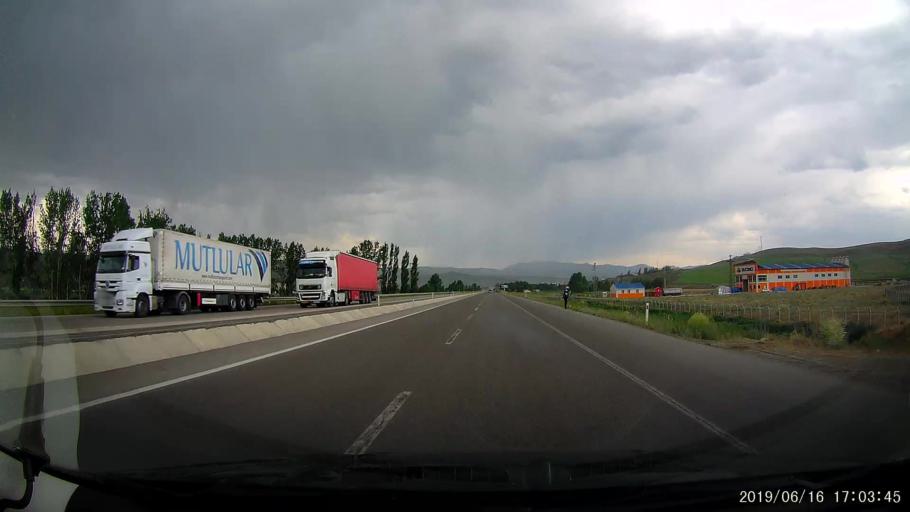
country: TR
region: Erzurum
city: Askale
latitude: 39.9334
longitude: 40.7245
